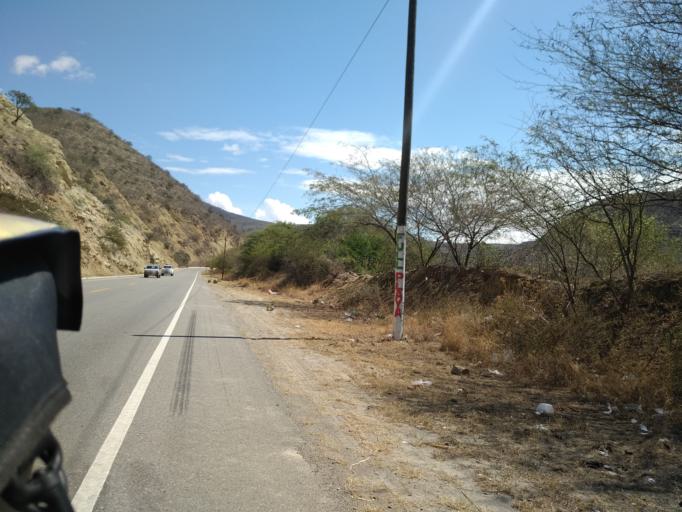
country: PE
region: Cajamarca
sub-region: Provincia de Cutervo
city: Choros
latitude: -5.8139
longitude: -78.7362
